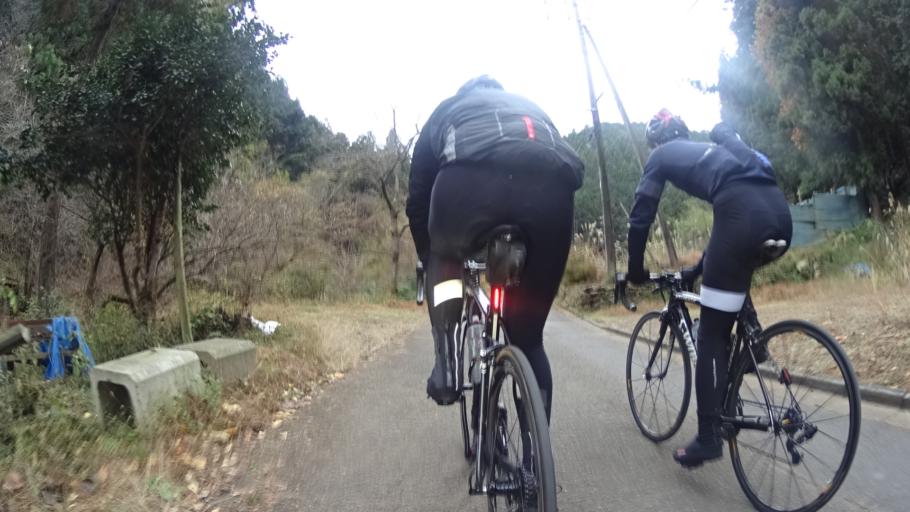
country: JP
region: Saitama
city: Morohongo
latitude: 35.9112
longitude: 139.2142
